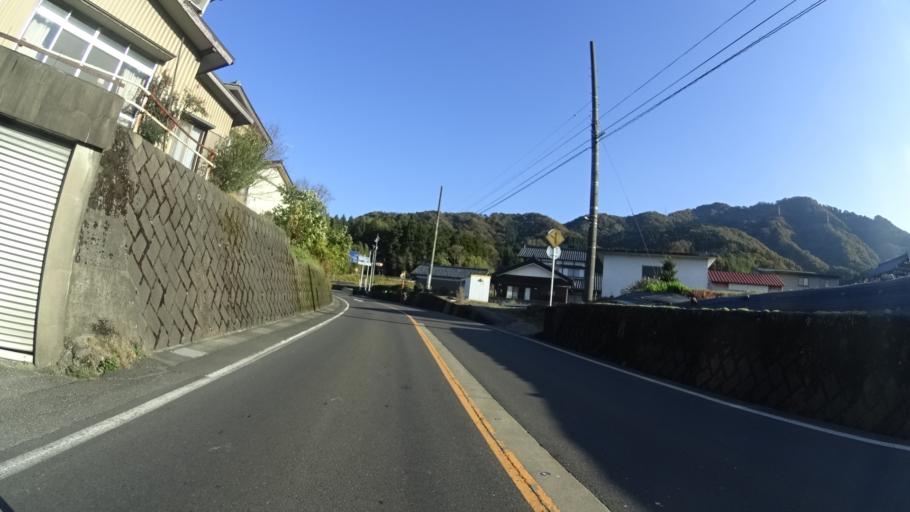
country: JP
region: Fukui
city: Maruoka
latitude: 36.1040
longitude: 136.3281
